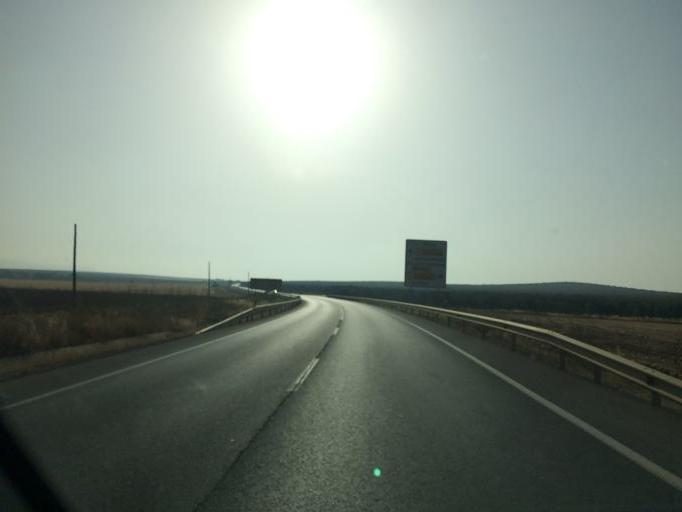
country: ES
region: Andalusia
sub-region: Provincia de Malaga
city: Humilladero
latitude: 37.0525
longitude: -4.7573
